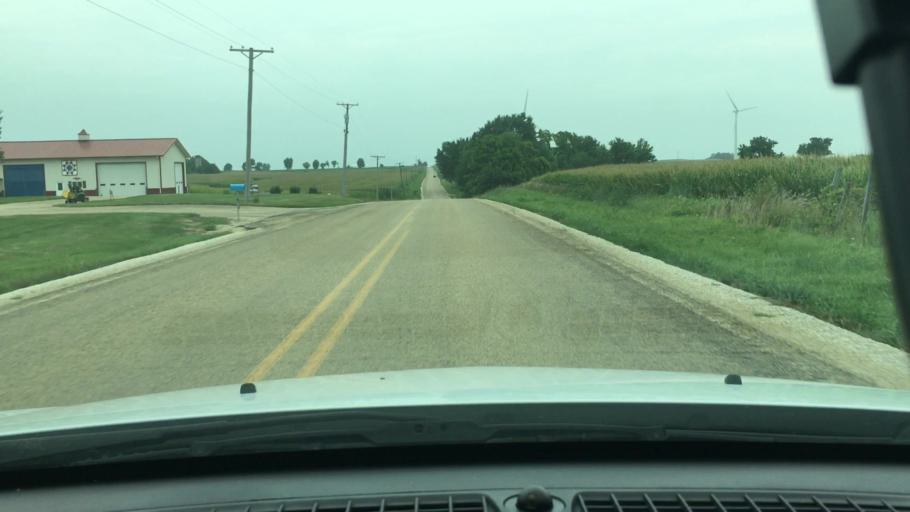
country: US
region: Illinois
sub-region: DeKalb County
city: Waterman
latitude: 41.8116
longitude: -88.7733
